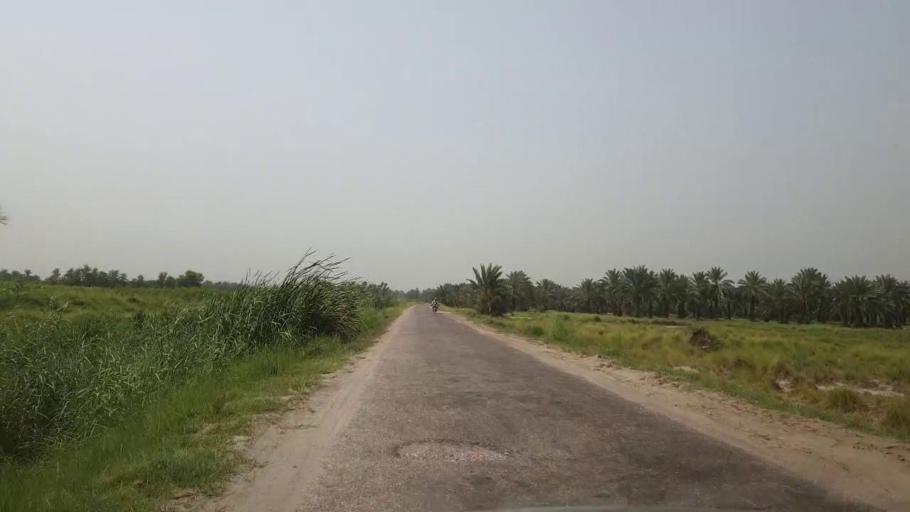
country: PK
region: Sindh
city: Gambat
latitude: 27.3839
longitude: 68.5485
